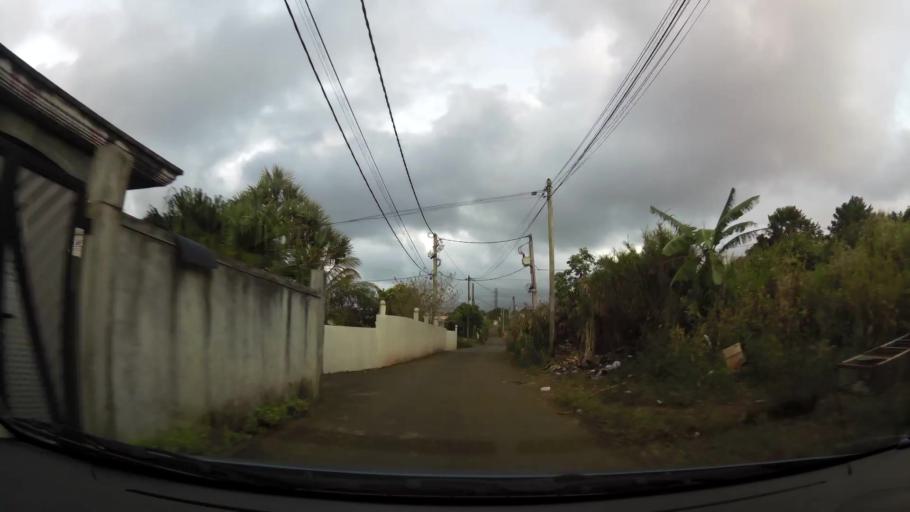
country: MU
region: Plaines Wilhems
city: Curepipe
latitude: -20.2990
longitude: 57.5327
